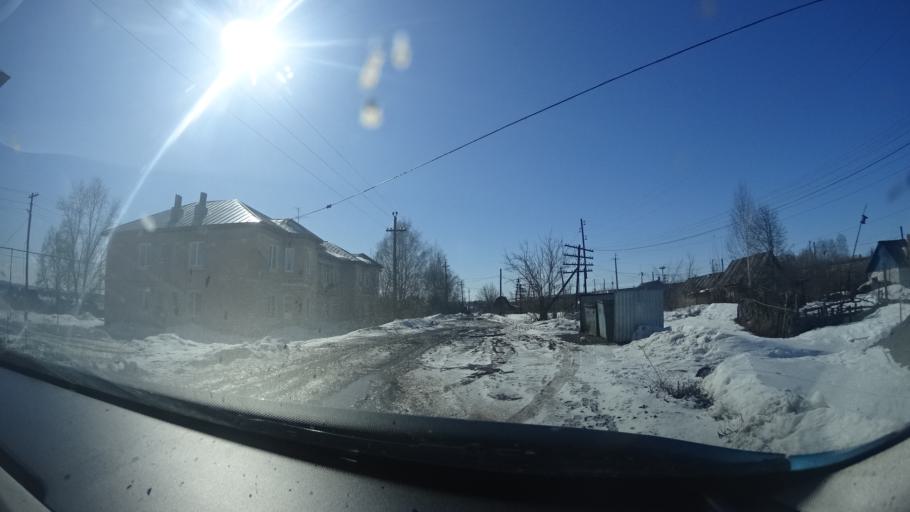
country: RU
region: Bashkortostan
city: Chishmy
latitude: 54.5841
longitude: 55.3935
